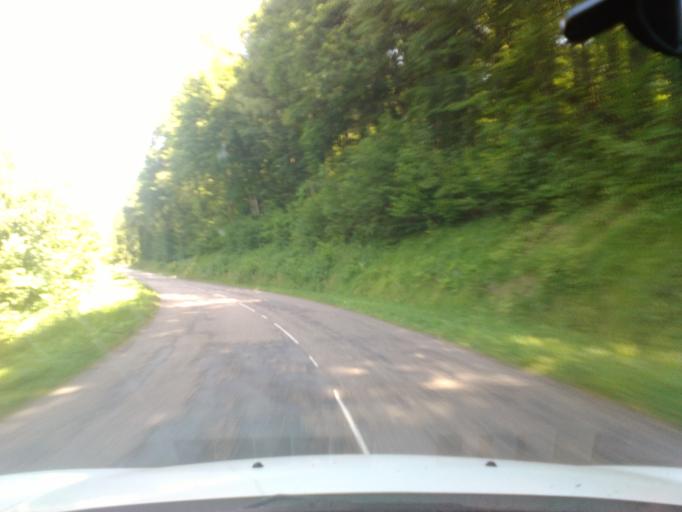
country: FR
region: Lorraine
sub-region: Departement des Vosges
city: Liffol-le-Grand
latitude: 48.3604
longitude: 5.6217
